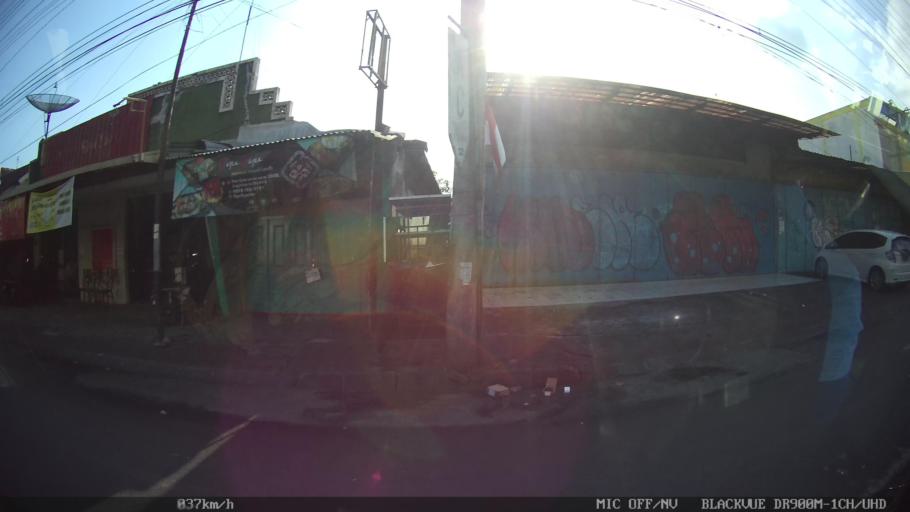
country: ID
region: Daerah Istimewa Yogyakarta
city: Yogyakarta
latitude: -7.7853
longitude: 110.3526
